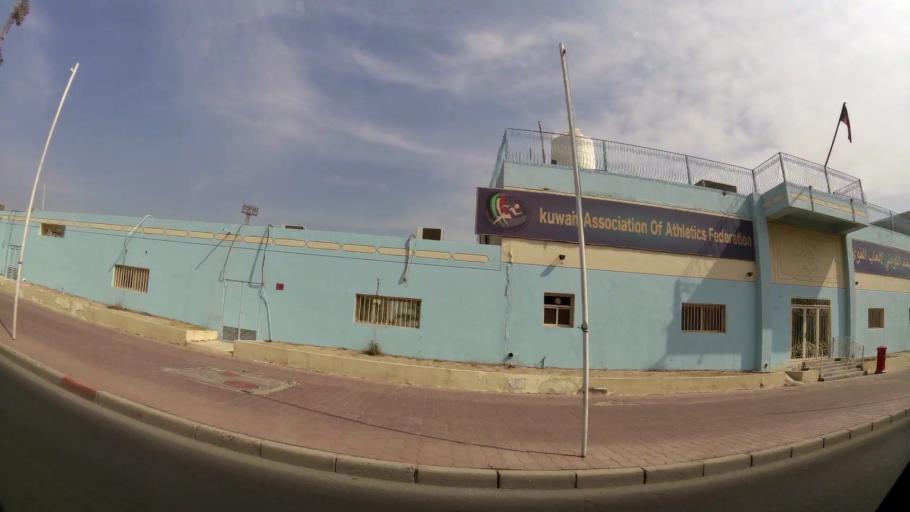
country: KW
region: Al Asimah
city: Ash Shamiyah
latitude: 29.3416
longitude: 47.9677
